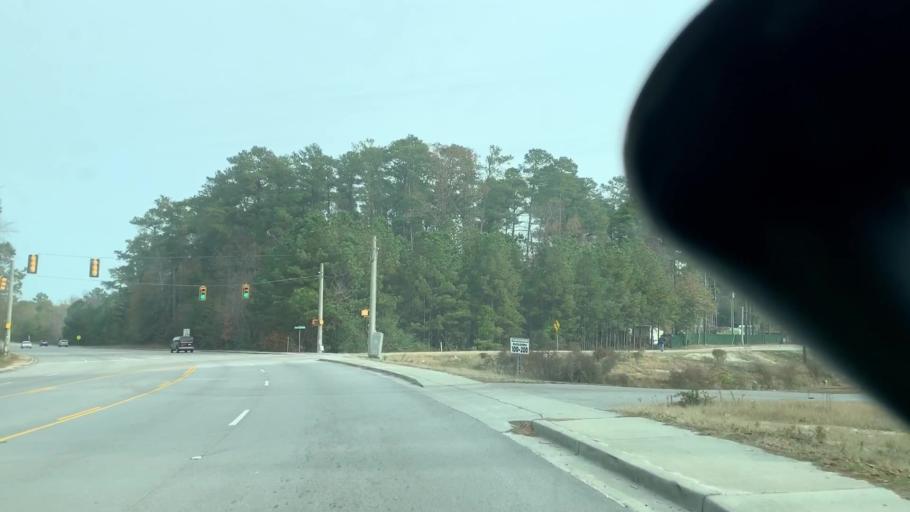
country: US
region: South Carolina
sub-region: Richland County
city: Dentsville
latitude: 34.0610
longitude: -80.9487
